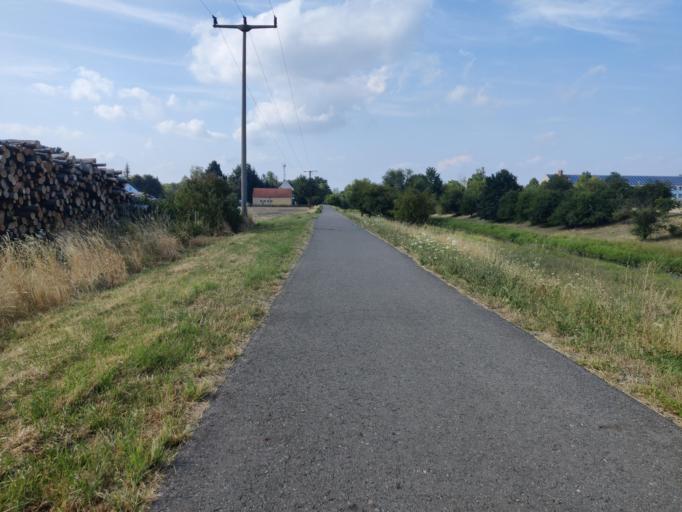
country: DE
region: Saxony
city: Deutzen
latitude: 51.1074
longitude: 12.4293
